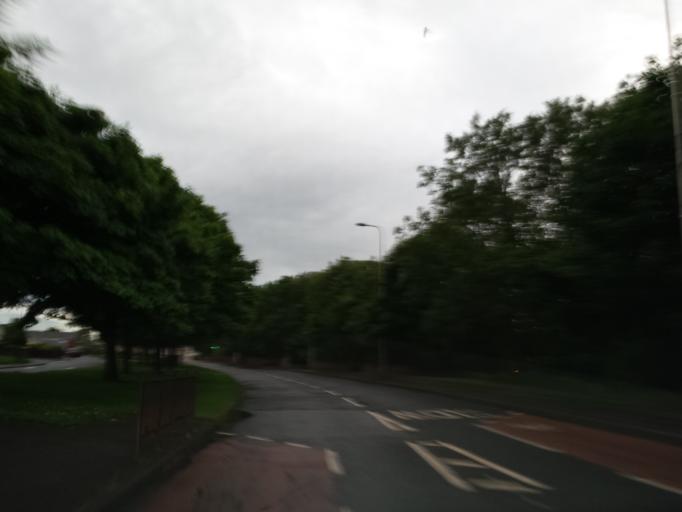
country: GB
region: Scotland
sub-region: East Lothian
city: Dunbar
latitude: 55.9951
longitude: -2.5488
